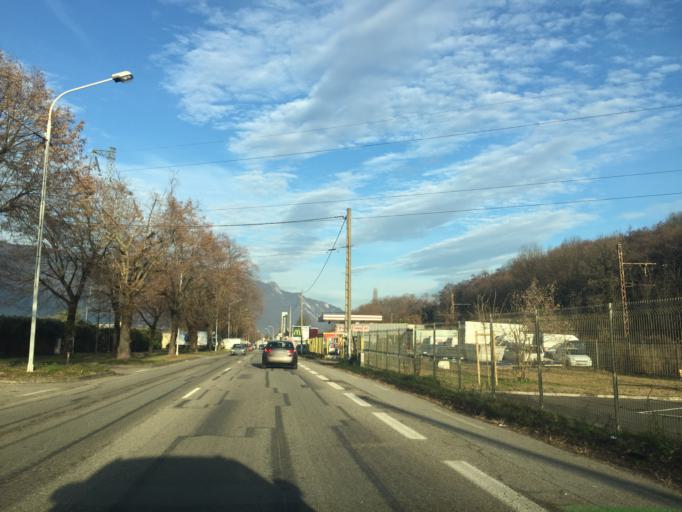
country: FR
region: Rhone-Alpes
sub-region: Departement de la Savoie
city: Cognin
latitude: 45.5902
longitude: 5.9043
